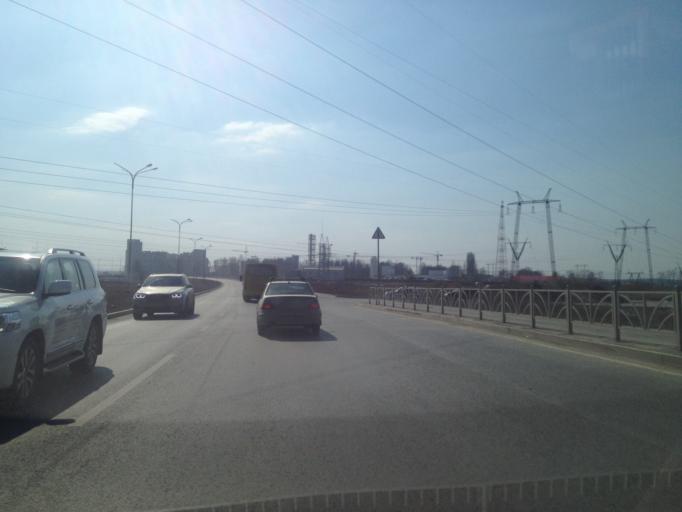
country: RU
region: Sverdlovsk
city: Sovkhoznyy
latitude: 56.7526
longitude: 60.5822
